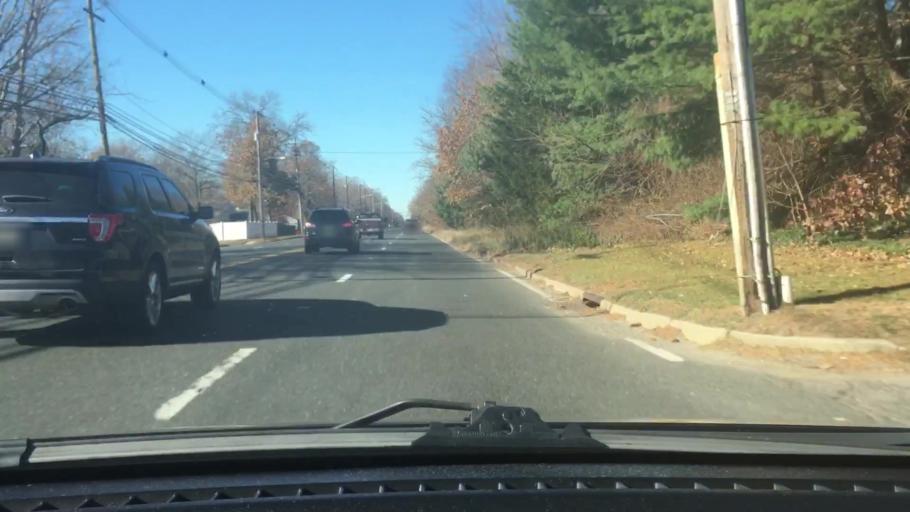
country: US
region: New Jersey
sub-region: Ocean County
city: Pine Lake Park
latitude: 40.0102
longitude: -74.2469
